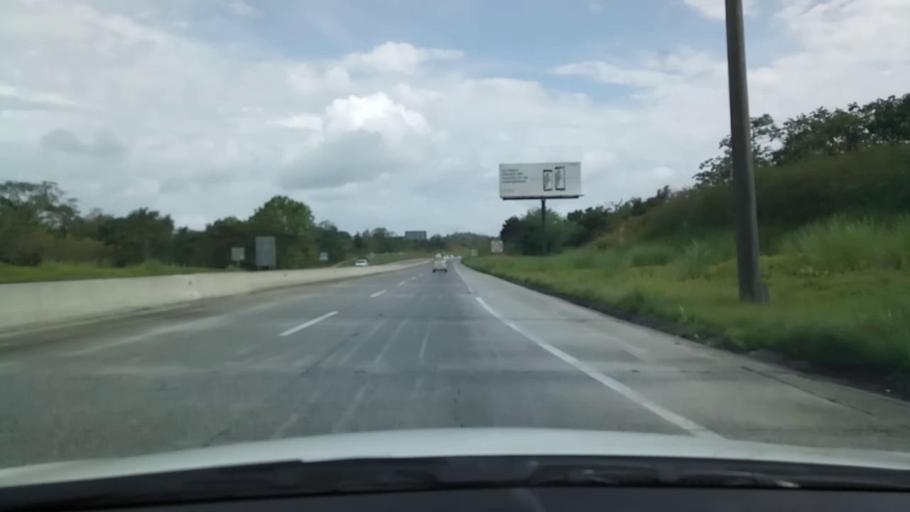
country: PA
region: Colon
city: Buena Vista
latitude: 9.2619
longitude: -79.6986
